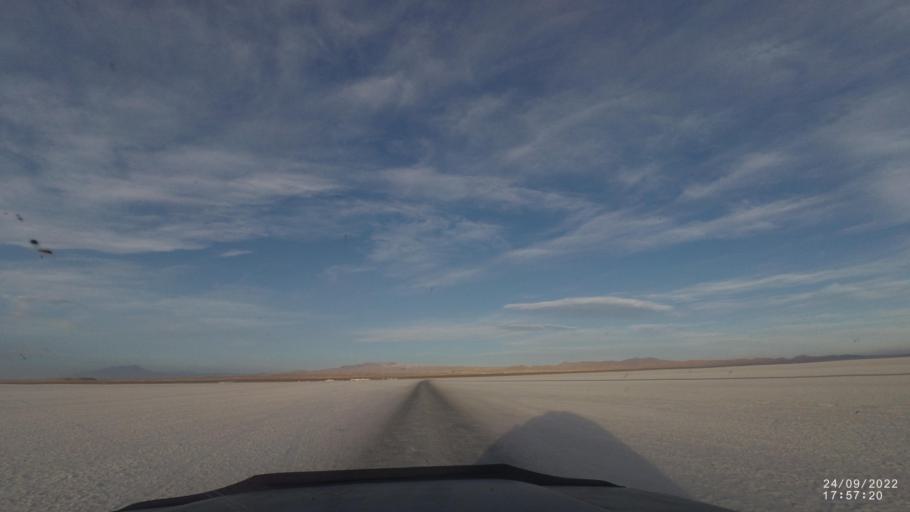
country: BO
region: Potosi
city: Colchani
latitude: -20.3209
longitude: -66.9946
